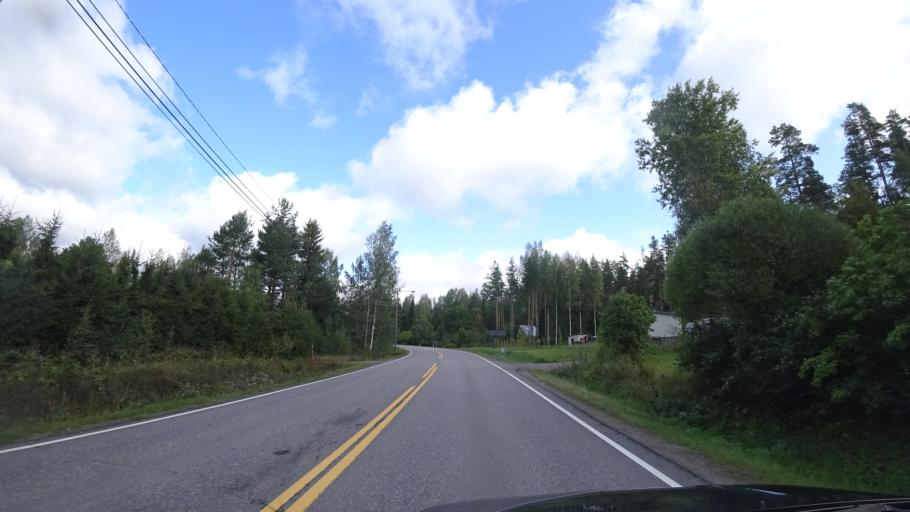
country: FI
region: Uusimaa
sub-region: Helsinki
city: Hyvinge
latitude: 60.6369
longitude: 25.0096
